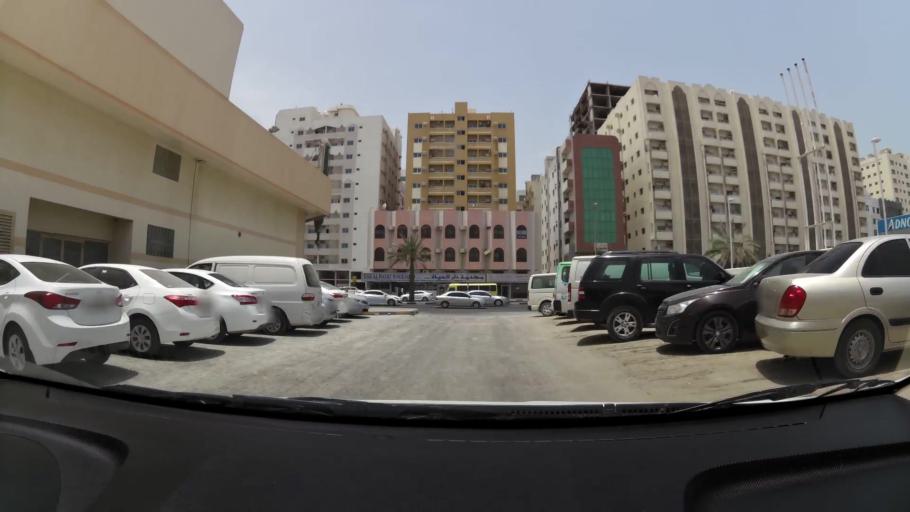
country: AE
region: Ash Shariqah
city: Sharjah
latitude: 25.3507
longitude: 55.3949
